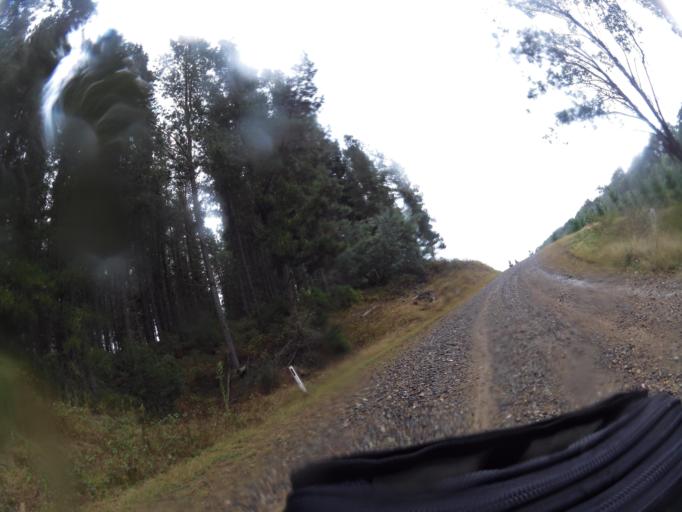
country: AU
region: New South Wales
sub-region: Greater Hume Shire
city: Holbrook
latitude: -36.2084
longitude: 147.5702
